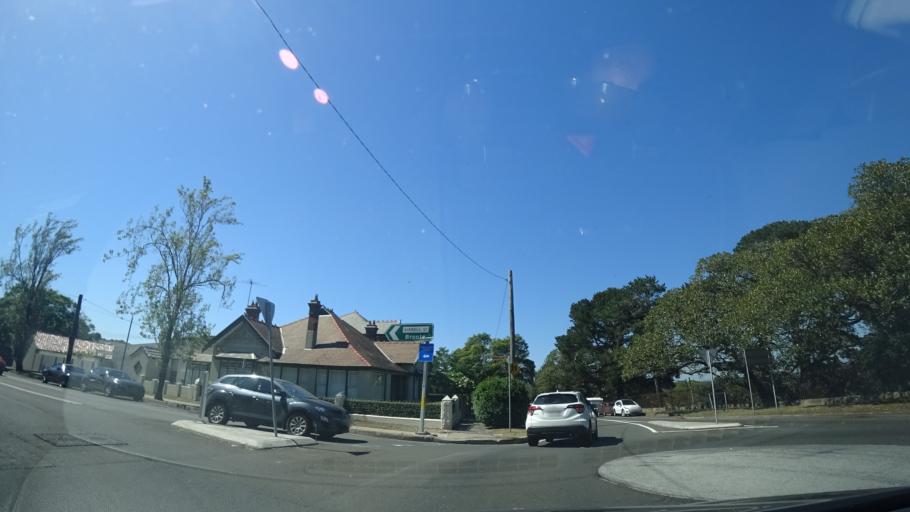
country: AU
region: New South Wales
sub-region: Waverley
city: Bondi Junction
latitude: -33.8947
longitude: 151.2409
